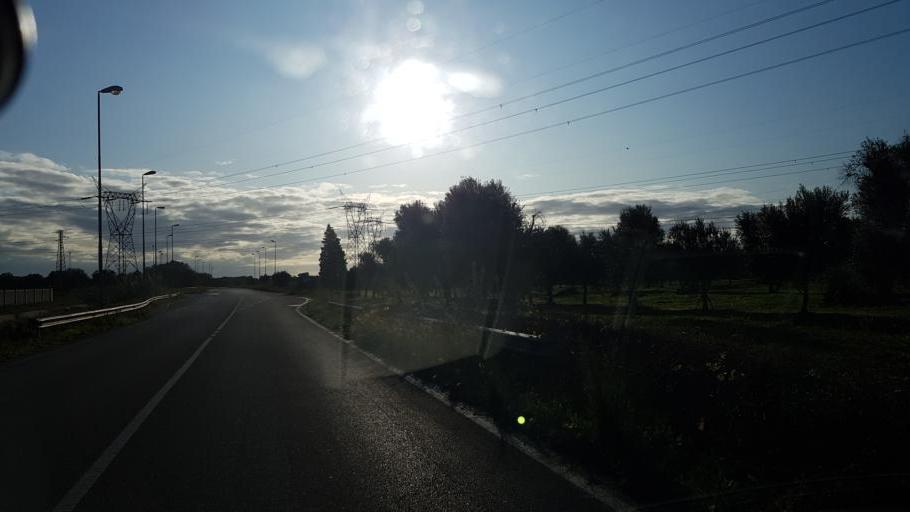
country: IT
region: Apulia
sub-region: Provincia di Brindisi
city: San Pietro Vernotico
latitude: 40.5566
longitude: 18.0270
